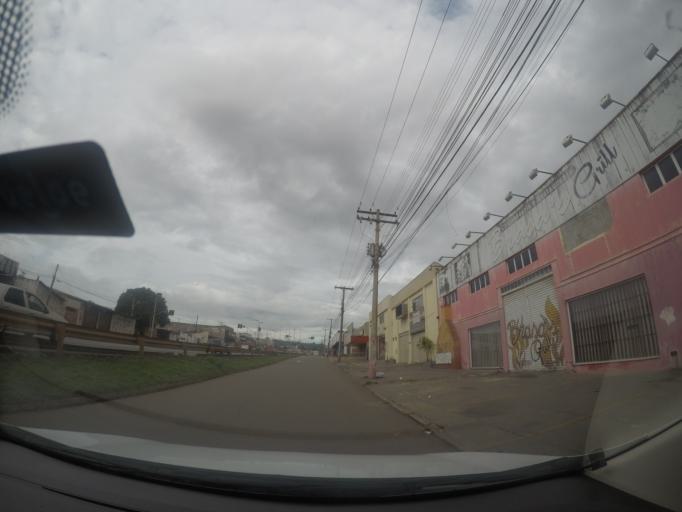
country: BR
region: Goias
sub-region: Goiania
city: Goiania
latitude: -16.6518
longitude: -49.3284
